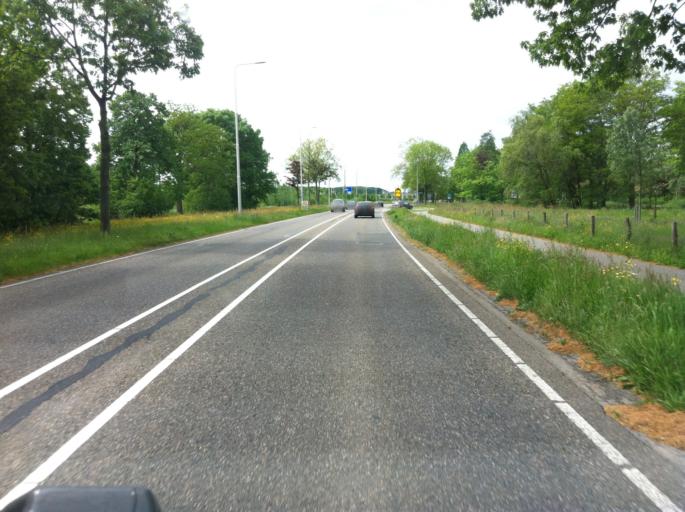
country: NL
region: Limburg
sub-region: Gemeente Roerdalen
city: Melick
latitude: 51.1855
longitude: 6.0246
